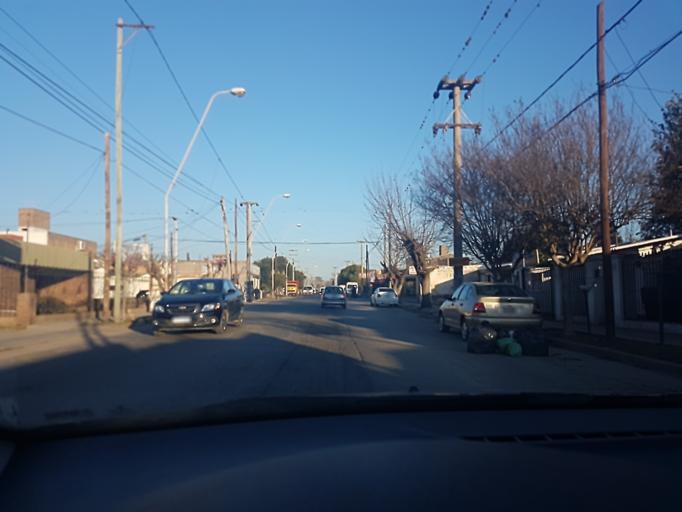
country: AR
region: Cordoba
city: Villa Allende
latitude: -31.3433
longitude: -64.2391
